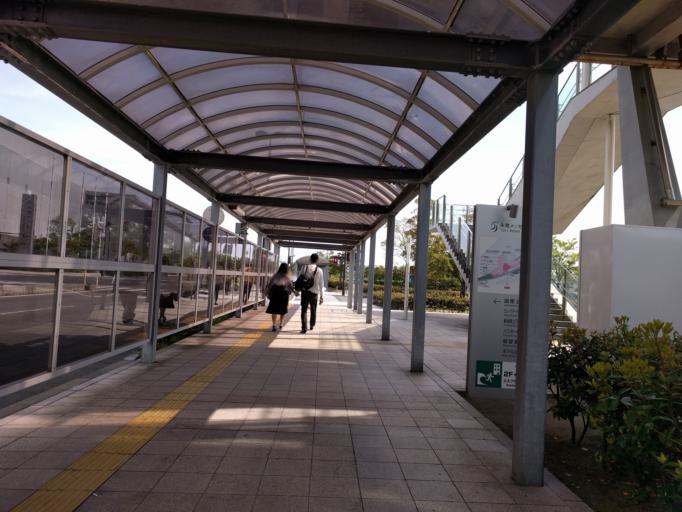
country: JP
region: Niigata
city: Niigata-shi
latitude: 37.9251
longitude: 139.0602
